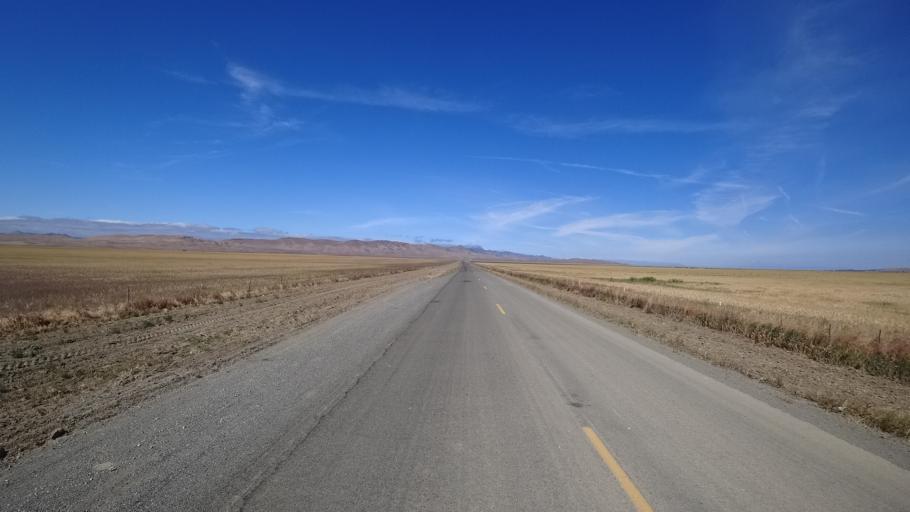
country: US
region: California
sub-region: Kings County
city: Avenal
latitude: 35.9351
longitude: -120.0580
